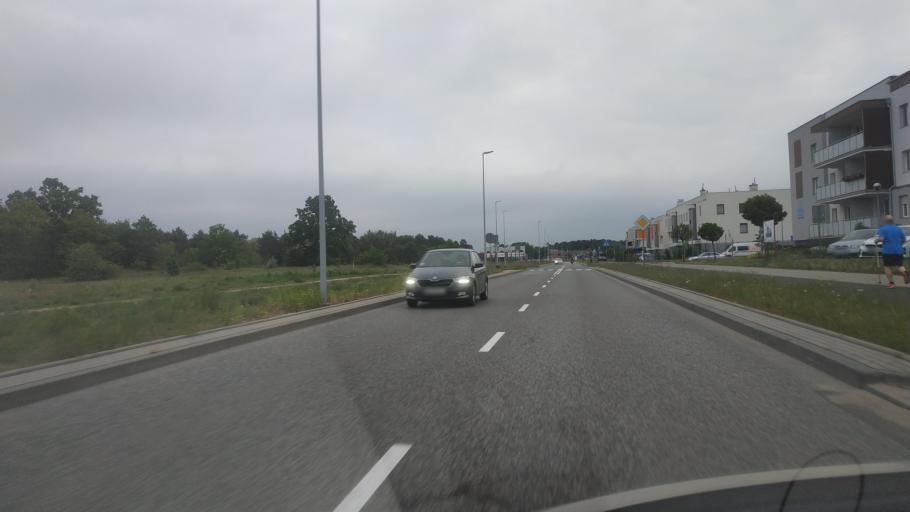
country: PL
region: Kujawsko-Pomorskie
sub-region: Torun
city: Torun
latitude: 53.0446
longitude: 18.6016
